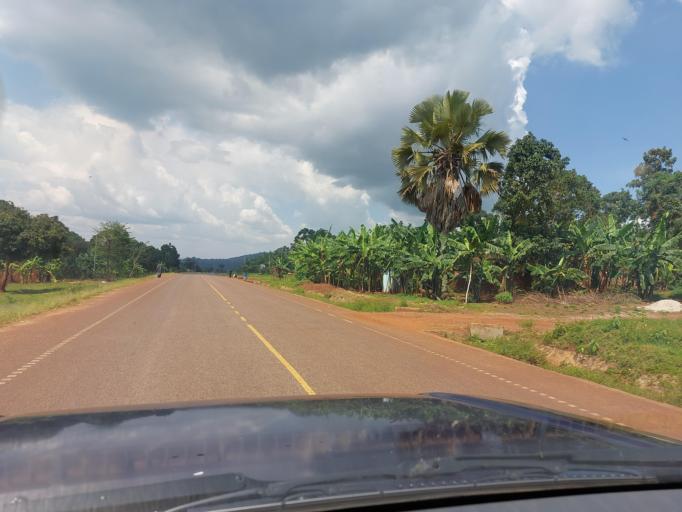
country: UG
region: Central Region
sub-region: Buikwe District
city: Njeru
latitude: 0.3312
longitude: 33.1187
